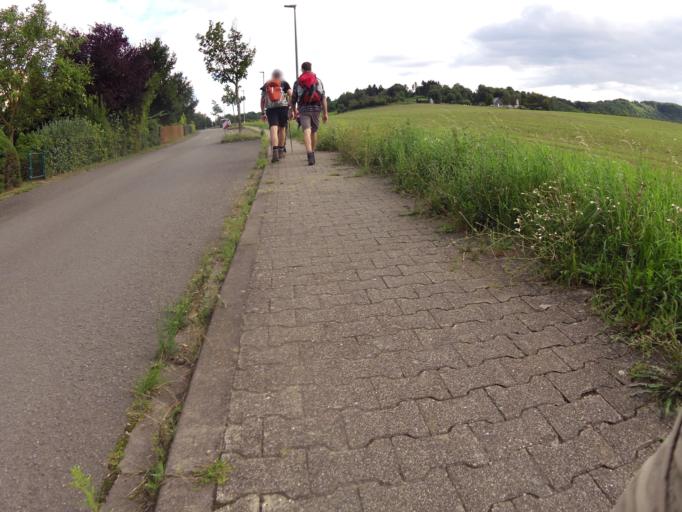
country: DE
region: Rheinland-Pfalz
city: Traisen
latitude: 49.8114
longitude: 7.8273
